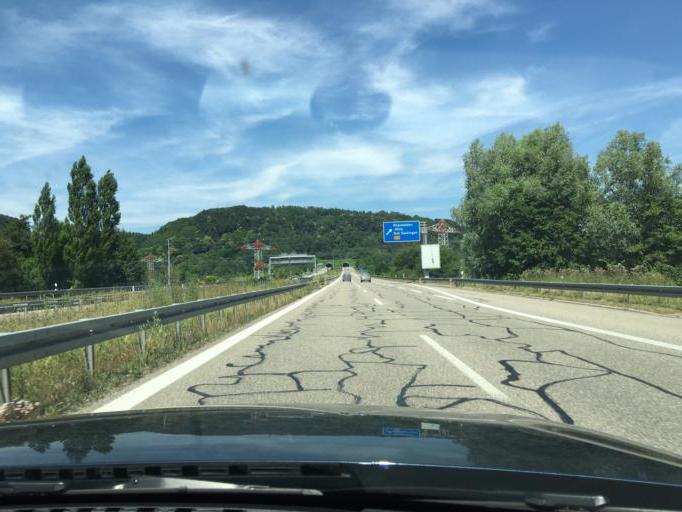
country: DE
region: Baden-Wuerttemberg
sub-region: Freiburg Region
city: Rheinfelden (Baden)
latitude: 47.5634
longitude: 7.7590
